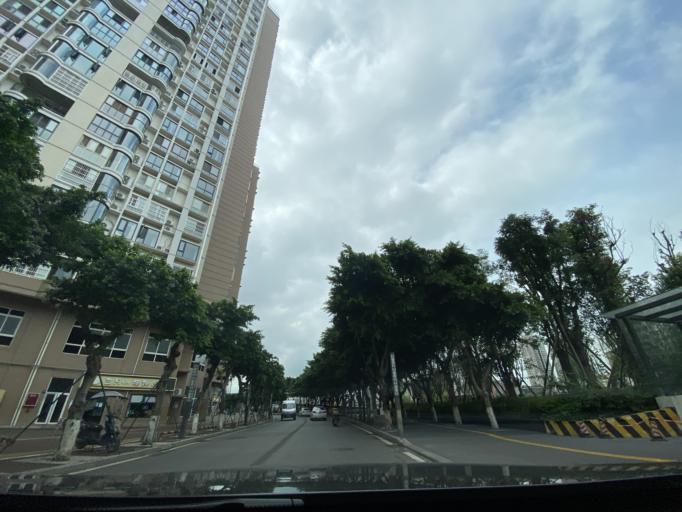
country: CN
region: Sichuan
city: Jiancheng
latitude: 30.3976
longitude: 104.5502
